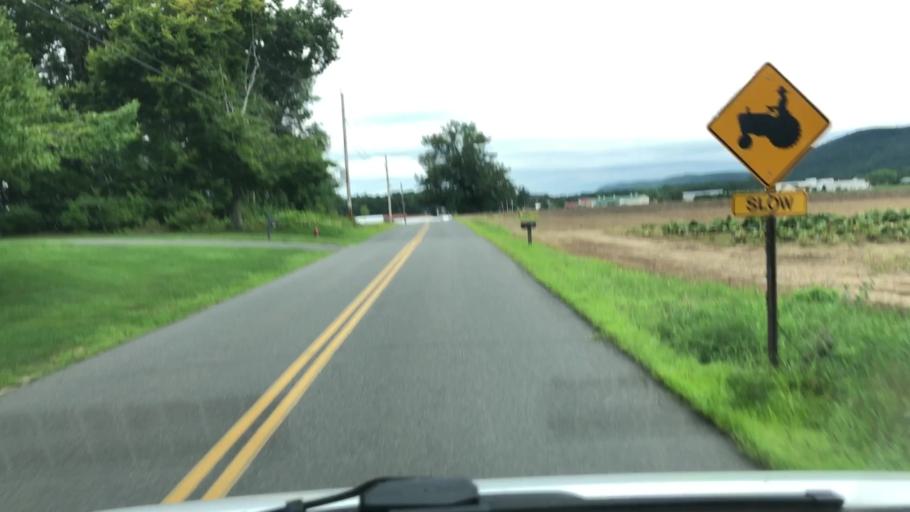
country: US
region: Massachusetts
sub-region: Franklin County
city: South Deerfield
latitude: 42.4548
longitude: -72.6092
